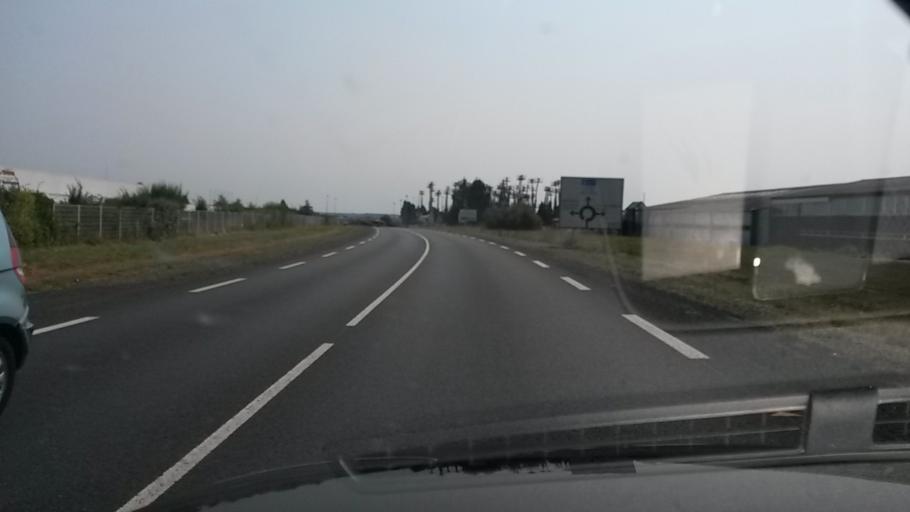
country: FR
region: Pays de la Loire
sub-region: Departement de la Loire-Atlantique
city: Mesanger
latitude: 47.4128
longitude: -1.1900
